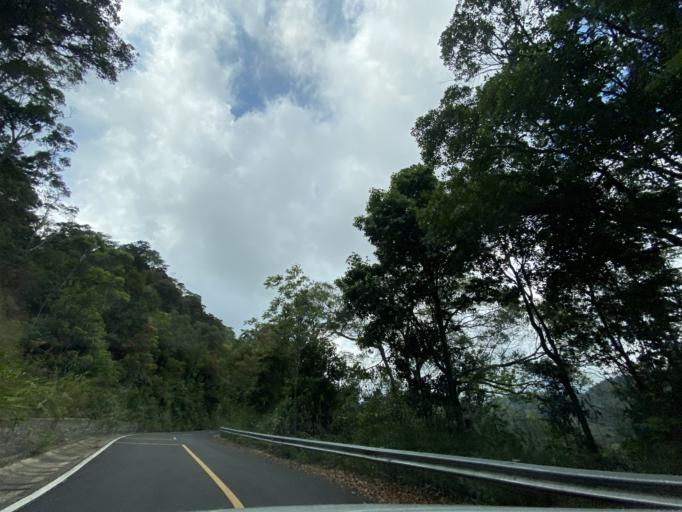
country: CN
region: Hainan
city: Diaoluoshan
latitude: 18.7074
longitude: 109.8837
